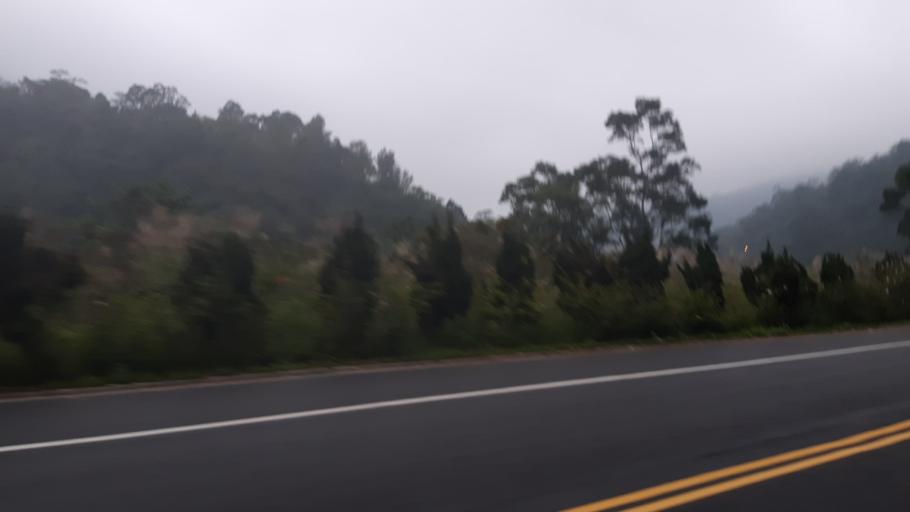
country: TW
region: Taiwan
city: Daxi
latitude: 24.6990
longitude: 121.1884
